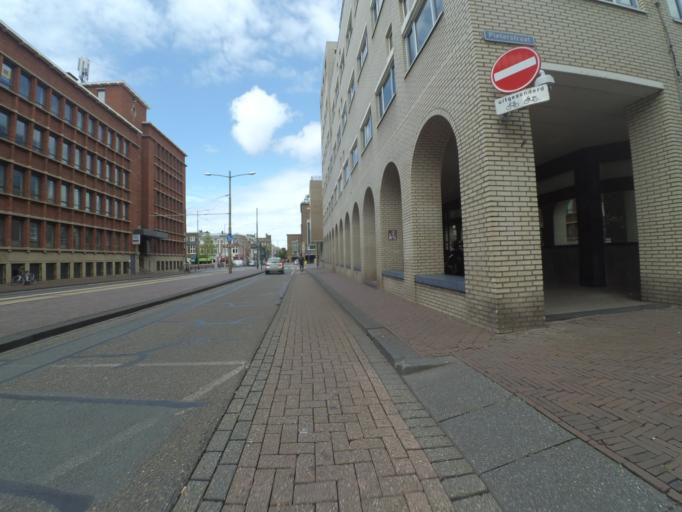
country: NL
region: South Holland
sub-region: Gemeente Den Haag
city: The Hague
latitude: 52.0793
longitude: 4.3034
